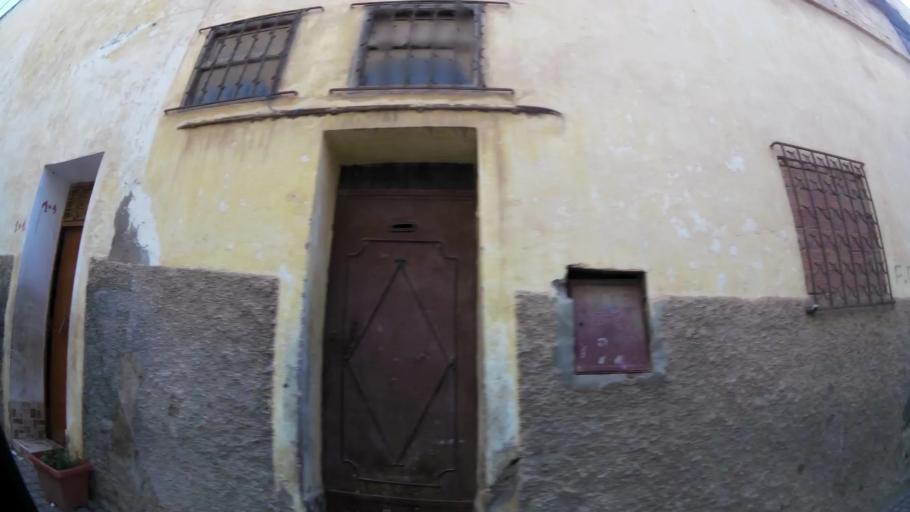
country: MA
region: Chaouia-Ouardigha
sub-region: Settat Province
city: Settat
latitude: 33.0099
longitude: -7.6253
